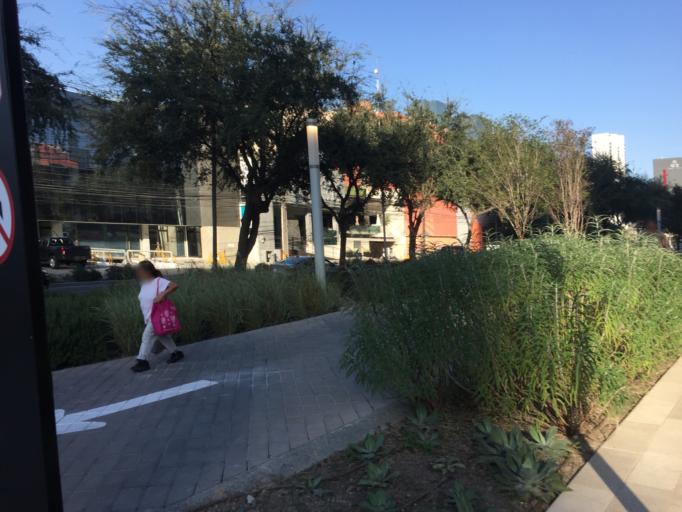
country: MX
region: Nuevo Leon
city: Garza Garcia
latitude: 25.6499
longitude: -100.3572
